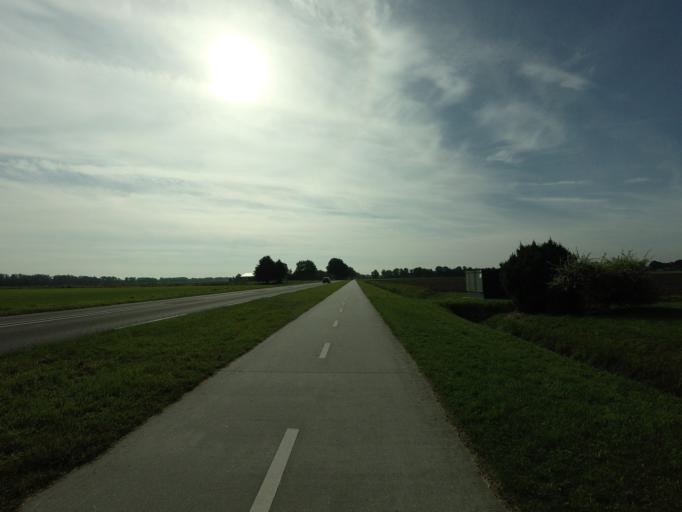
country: NL
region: Drenthe
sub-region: Gemeente Aa en Hunze
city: Anloo
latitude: 52.9542
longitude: 6.6647
